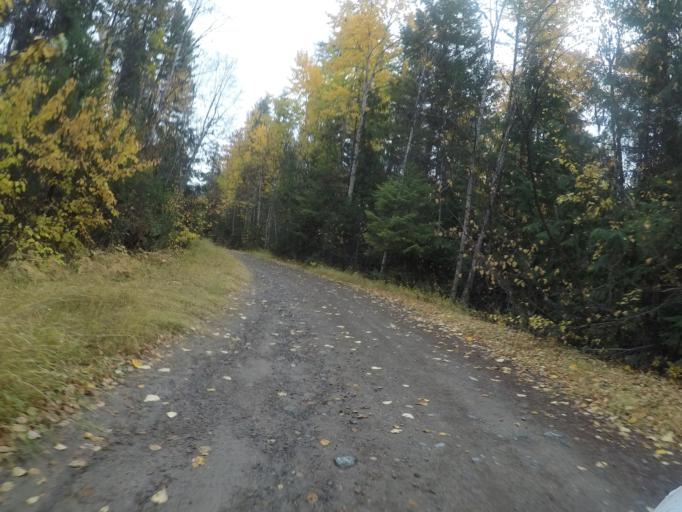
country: US
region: Montana
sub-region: Flathead County
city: Bigfork
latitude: 47.8781
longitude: -113.8776
